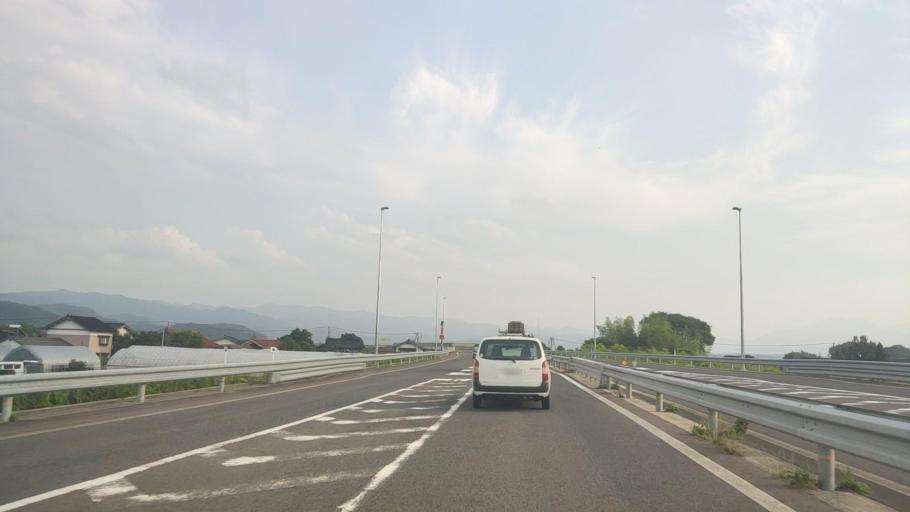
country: JP
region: Tottori
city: Kurayoshi
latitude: 35.4450
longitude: 133.8074
